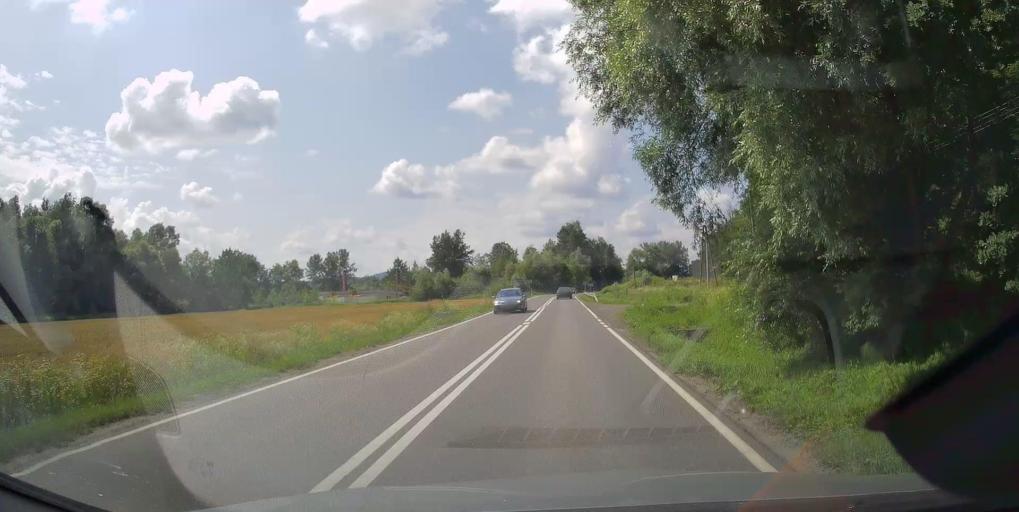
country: PL
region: Lesser Poland Voivodeship
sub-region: Powiat tarnowski
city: Janowice
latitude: 49.8796
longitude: 20.8312
